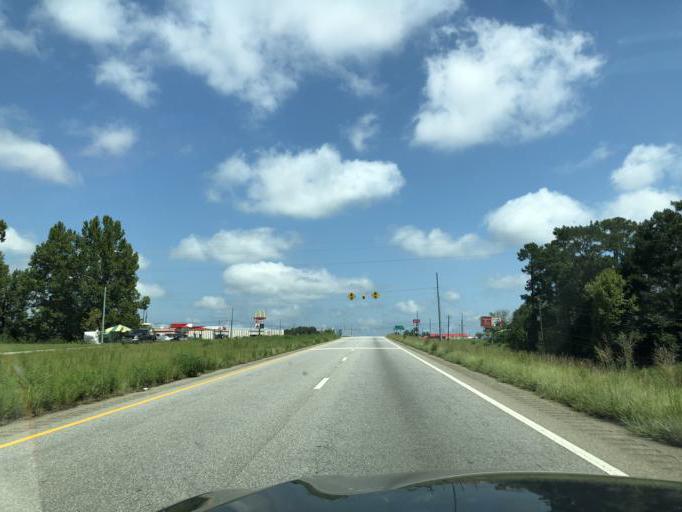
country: US
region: Alabama
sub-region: Henry County
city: Abbeville
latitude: 31.5479
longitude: -85.2855
